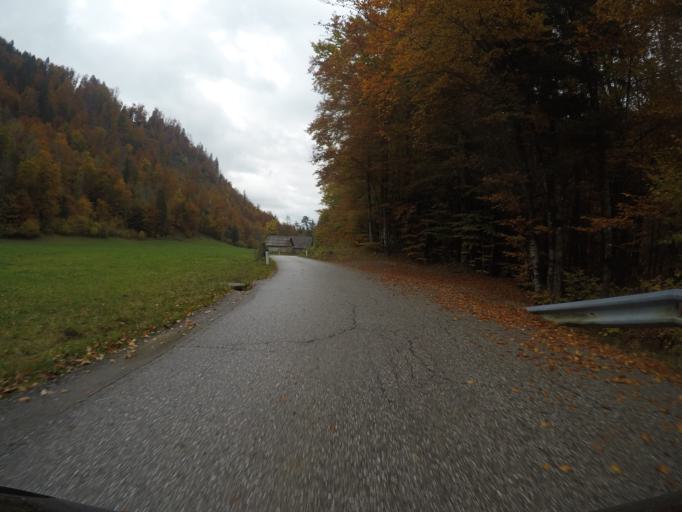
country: SI
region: Gorje
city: Zgornje Gorje
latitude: 46.3896
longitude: 14.0249
